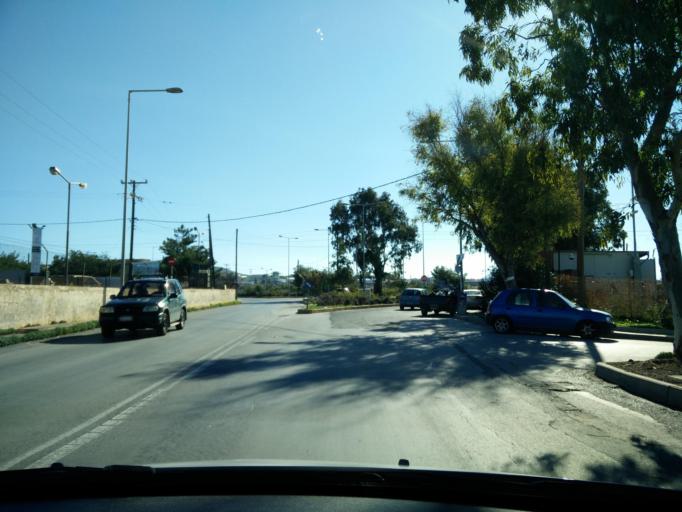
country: GR
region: Crete
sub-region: Nomos Irakleiou
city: Nea Alikarnassos
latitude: 35.3337
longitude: 25.1655
